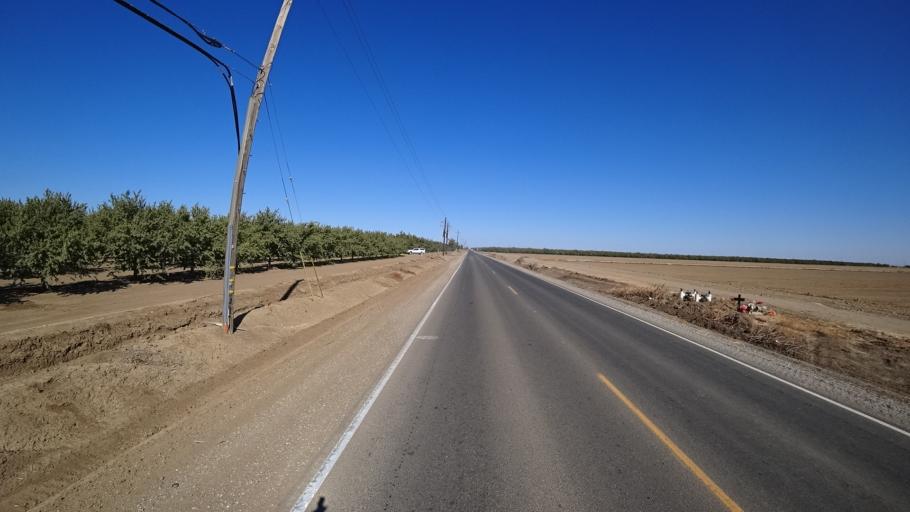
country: US
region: California
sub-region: Yolo County
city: Winters
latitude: 38.5573
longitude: -121.9713
